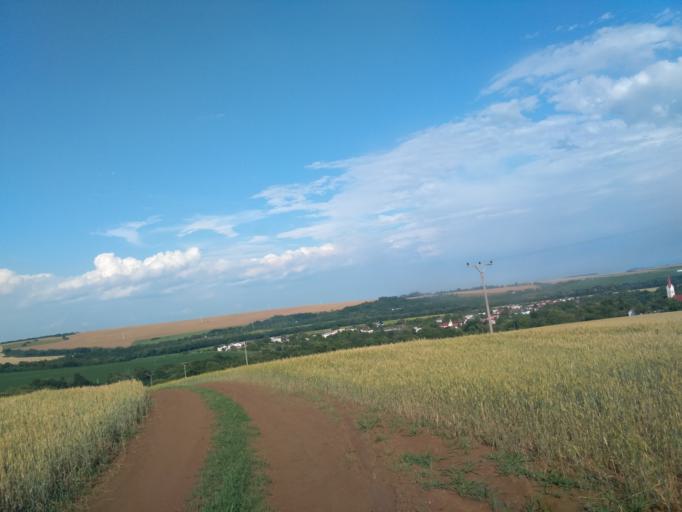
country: SK
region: Kosicky
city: Secovce
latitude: 48.6016
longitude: 21.5443
